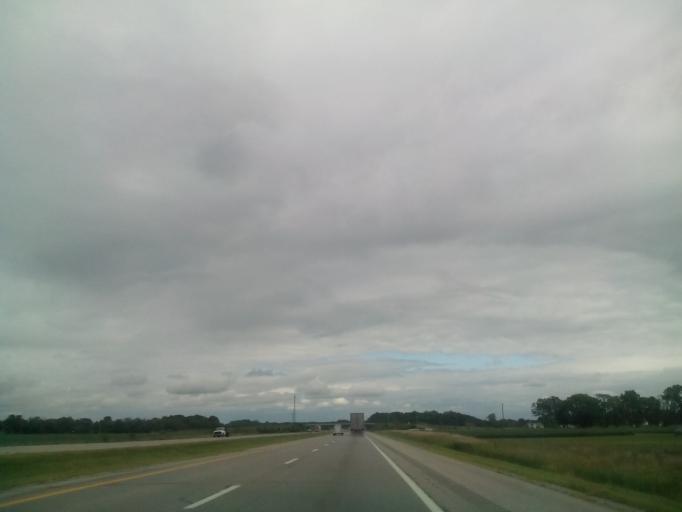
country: US
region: Ohio
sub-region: Fulton County
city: Burlington
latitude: 41.5929
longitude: -84.3582
